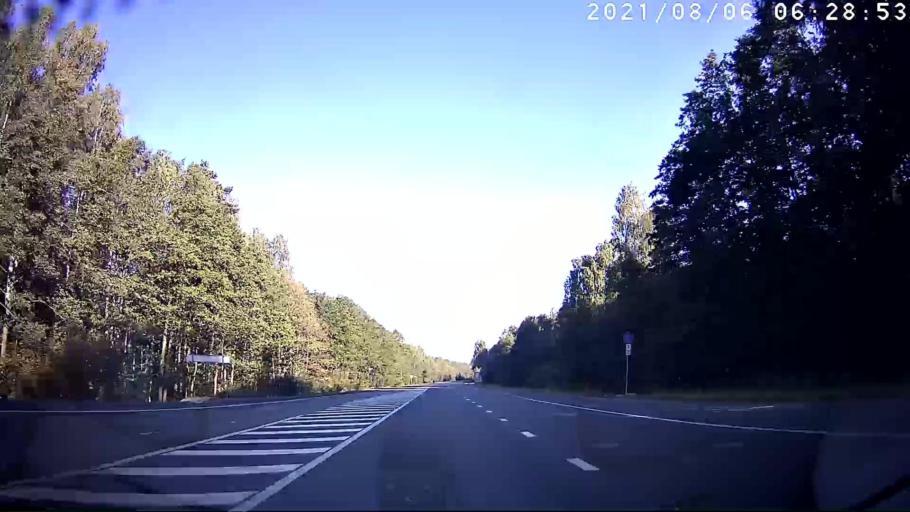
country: RU
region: Mariy-El
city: Krasnogorskiy
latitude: 56.1497
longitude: 48.3054
